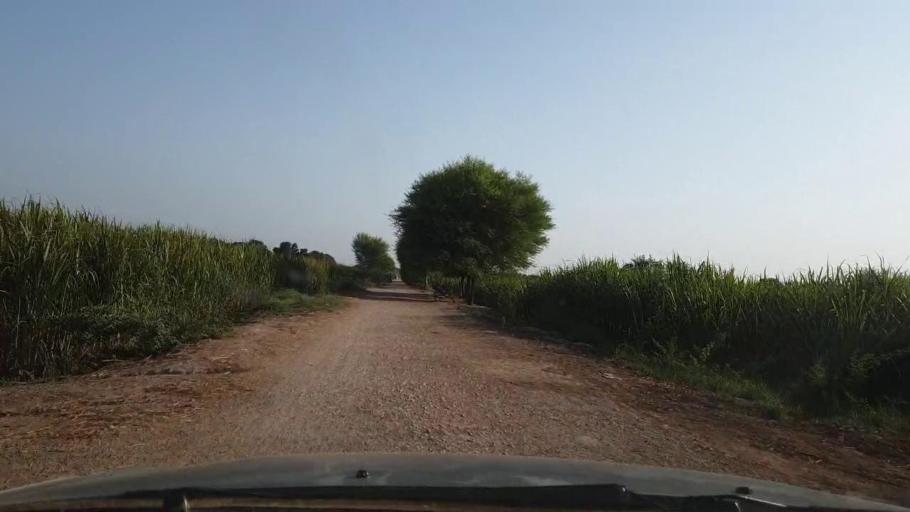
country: PK
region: Sindh
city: Tando Ghulam Ali
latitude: 25.1283
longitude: 68.9407
